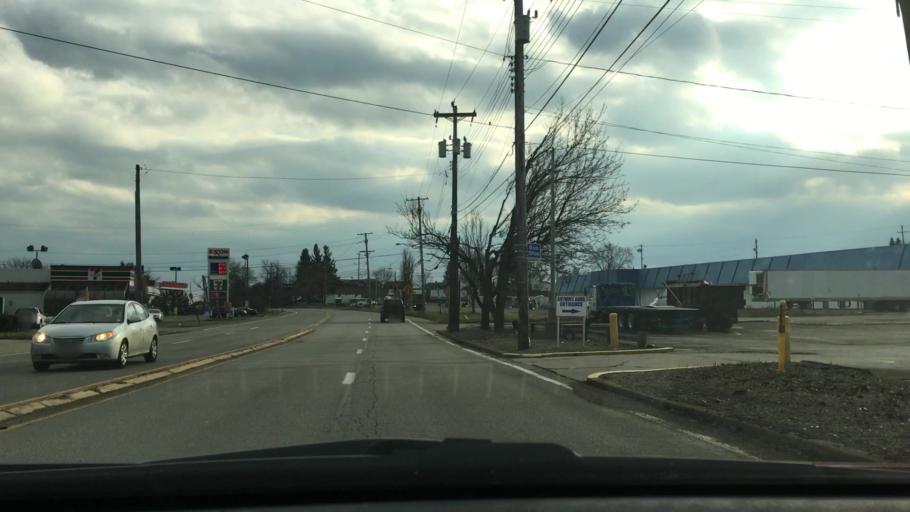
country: US
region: Pennsylvania
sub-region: Allegheny County
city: Pleasant Hills
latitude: 40.3498
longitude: -79.9271
